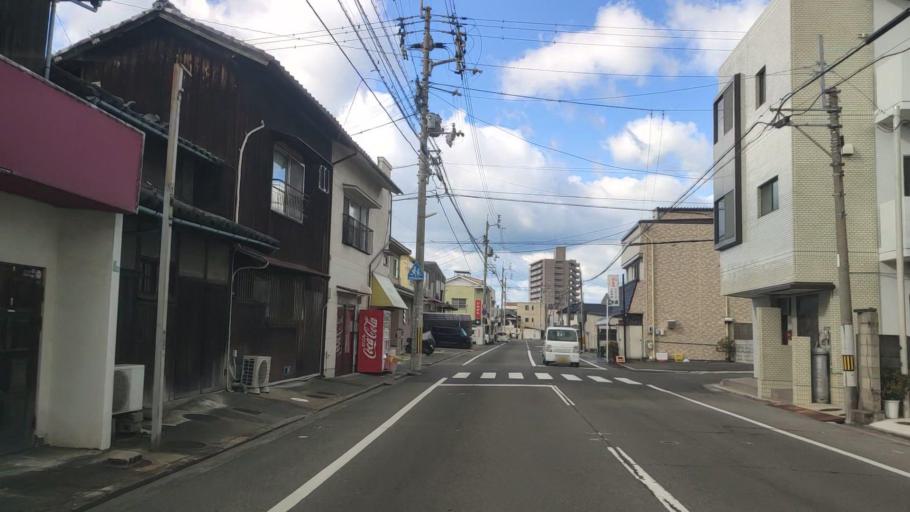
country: JP
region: Ehime
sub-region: Shikoku-chuo Shi
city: Matsuyama
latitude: 33.8645
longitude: 132.7174
